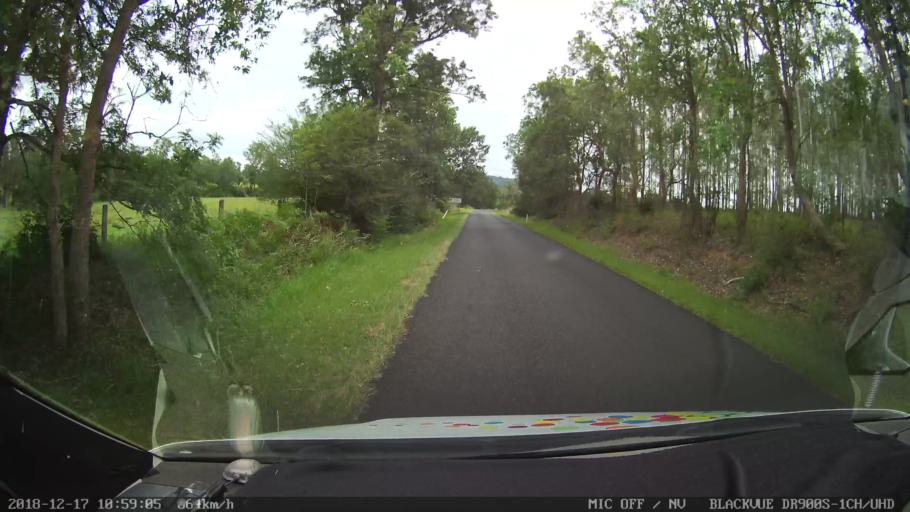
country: AU
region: New South Wales
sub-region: Richmond Valley
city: Casino
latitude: -28.8233
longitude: 152.6091
